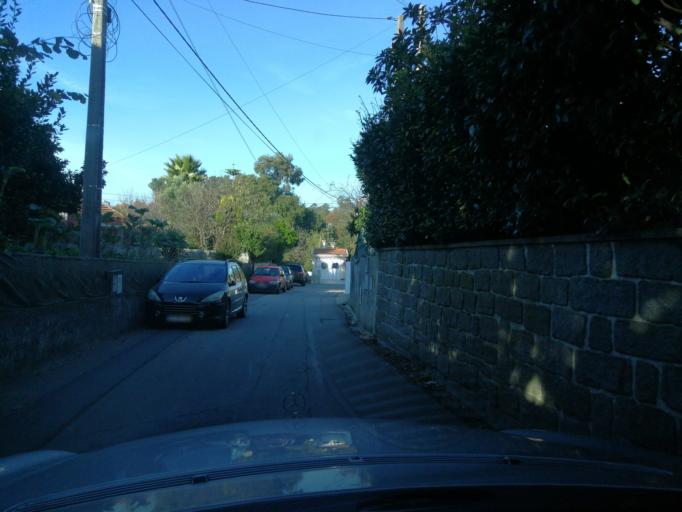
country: PT
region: Braga
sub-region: Vila Nova de Famalicao
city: Vila Nova de Famalicao
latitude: 41.4263
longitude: -8.5193
